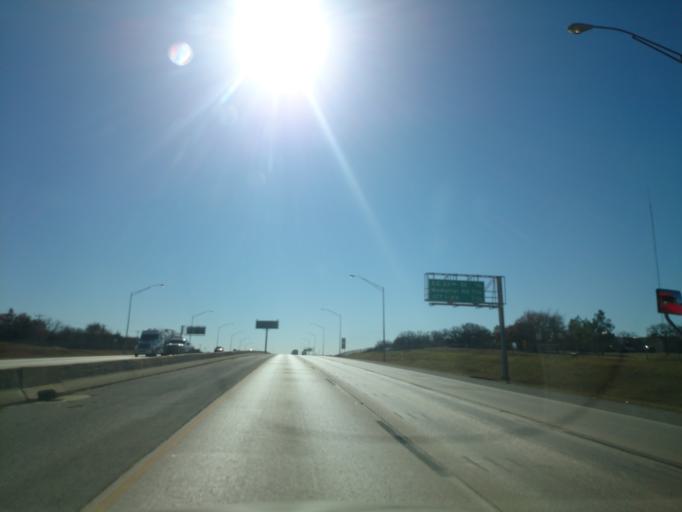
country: US
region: Oklahoma
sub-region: Oklahoma County
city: Edmond
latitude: 35.6318
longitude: -97.4249
